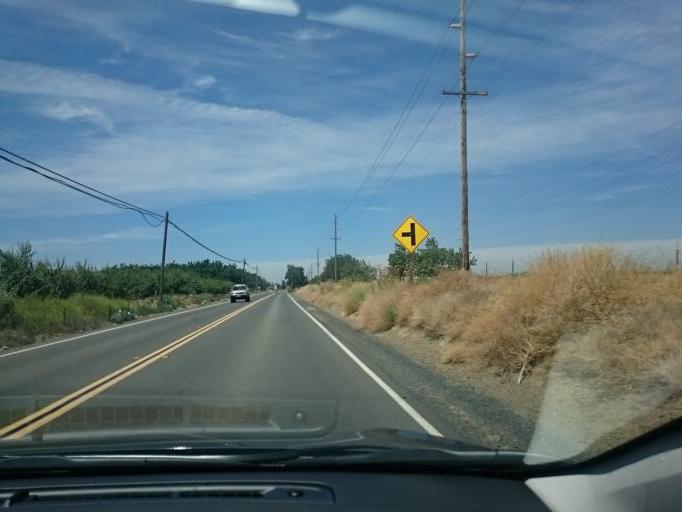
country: US
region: California
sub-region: Stanislaus County
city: Waterford
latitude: 37.6466
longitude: -120.6701
